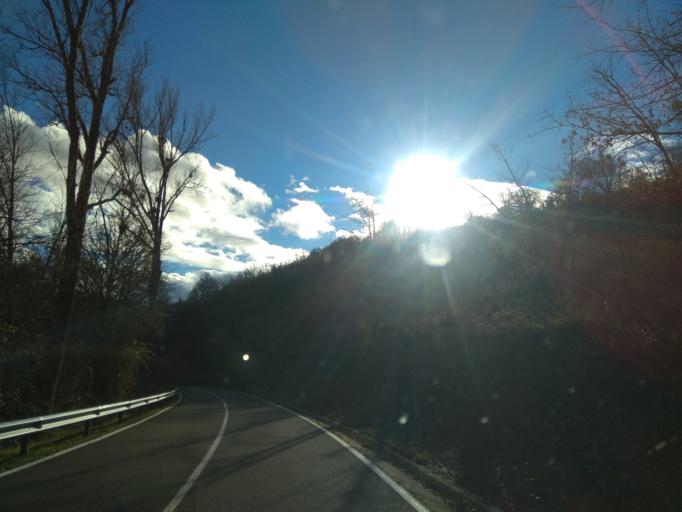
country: ES
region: Cantabria
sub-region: Provincia de Cantabria
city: San Martin de Elines
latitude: 42.8845
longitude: -3.9112
